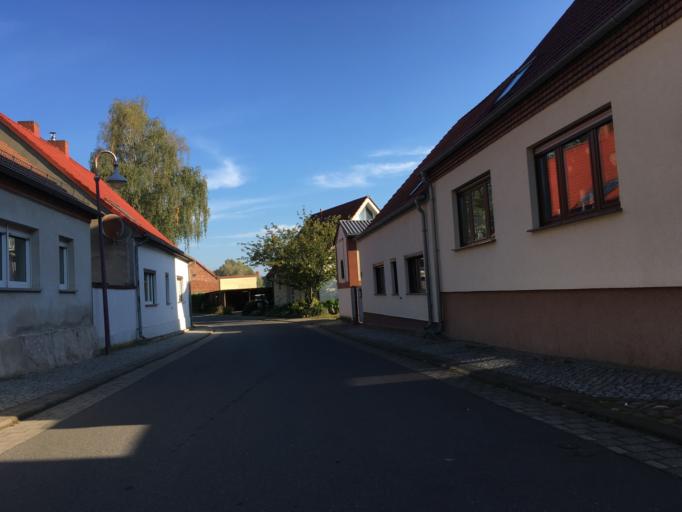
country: DE
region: Brandenburg
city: Lebus
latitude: 52.4271
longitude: 14.5431
